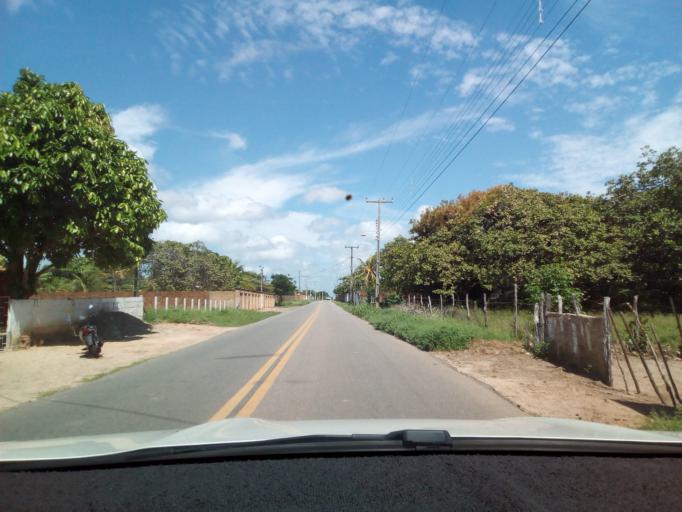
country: BR
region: Ceara
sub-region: Beberibe
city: Beberibe
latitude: -4.1844
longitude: -38.0991
